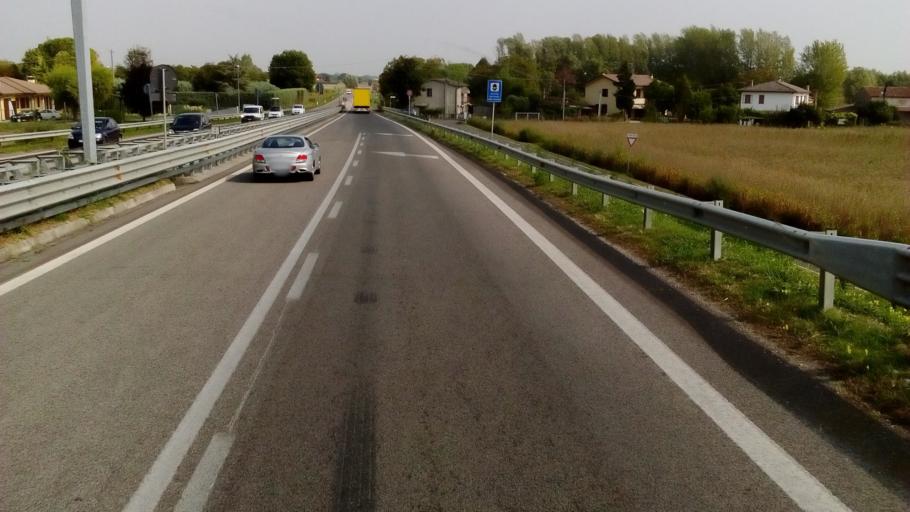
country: IT
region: Veneto
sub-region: Provincia di Padova
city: Monselice
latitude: 45.2099
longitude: 11.7610
